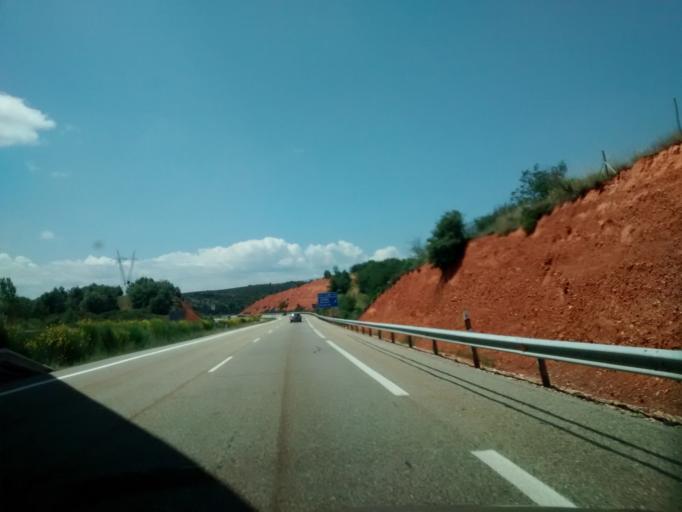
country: ES
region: Castille and Leon
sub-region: Provincia de Leon
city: Brazuelo
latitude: 42.4997
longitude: -6.1231
